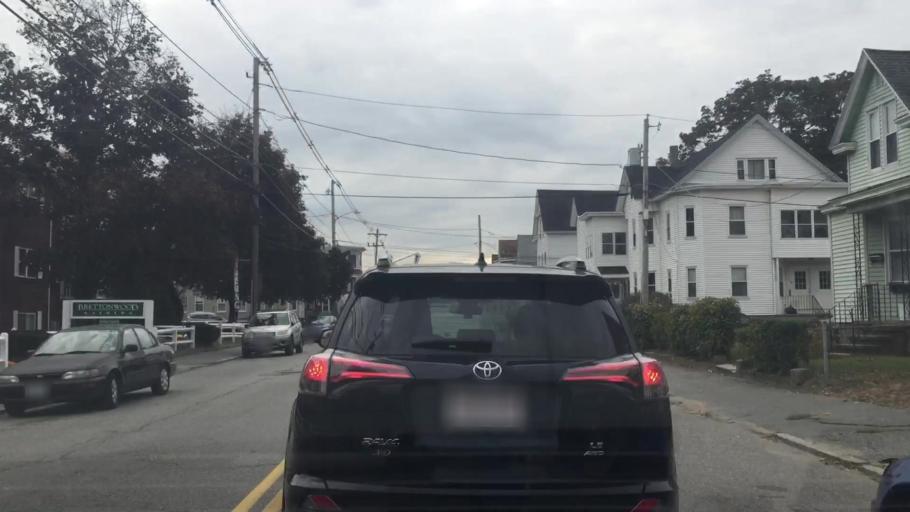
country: US
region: Massachusetts
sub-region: Middlesex County
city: Dracut
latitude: 42.6596
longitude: -71.3155
